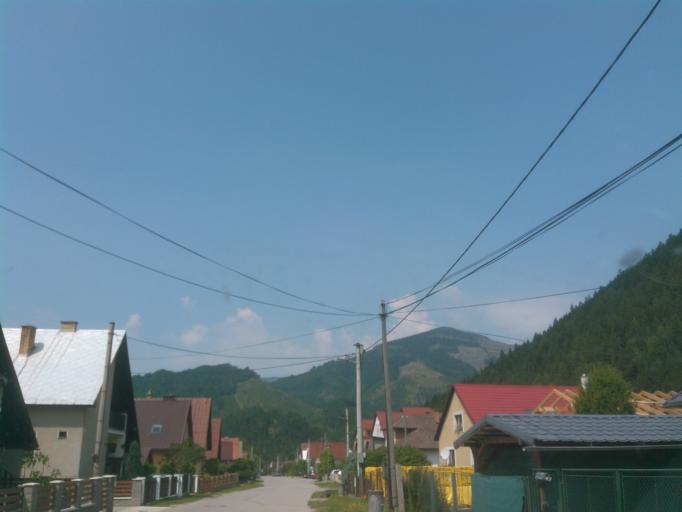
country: SK
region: Zilinsky
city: Ruzomberok
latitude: 48.9498
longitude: 19.2734
